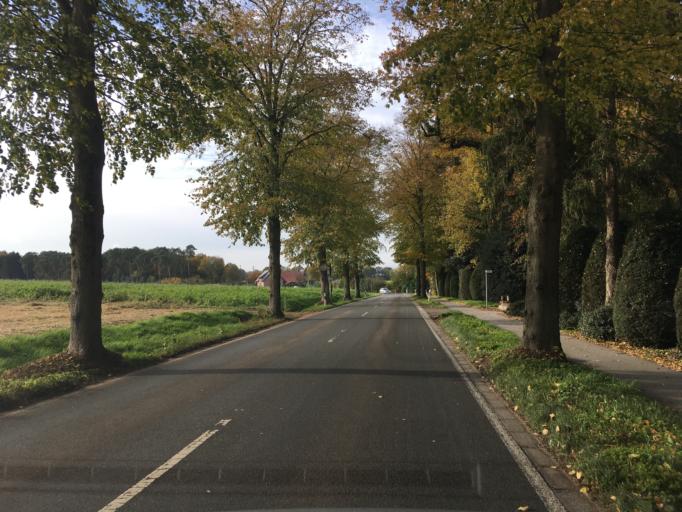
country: DE
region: North Rhine-Westphalia
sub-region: Regierungsbezirk Munster
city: Klein Reken
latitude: 51.8458
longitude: 7.0764
